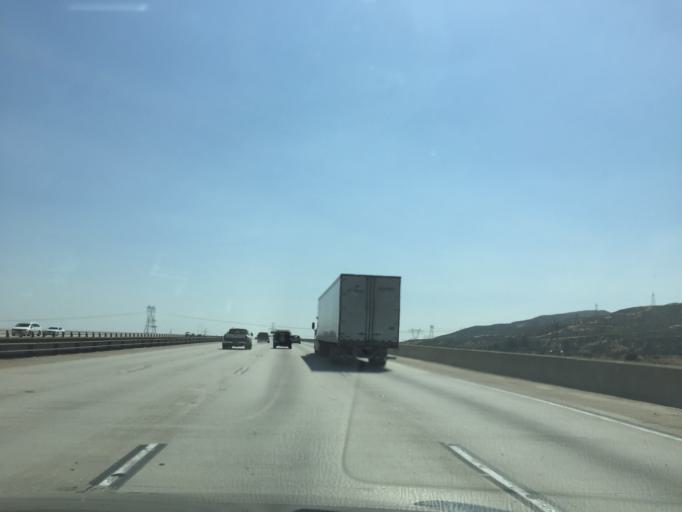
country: US
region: California
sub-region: San Bernardino County
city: Muscoy
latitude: 34.1879
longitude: -117.4297
